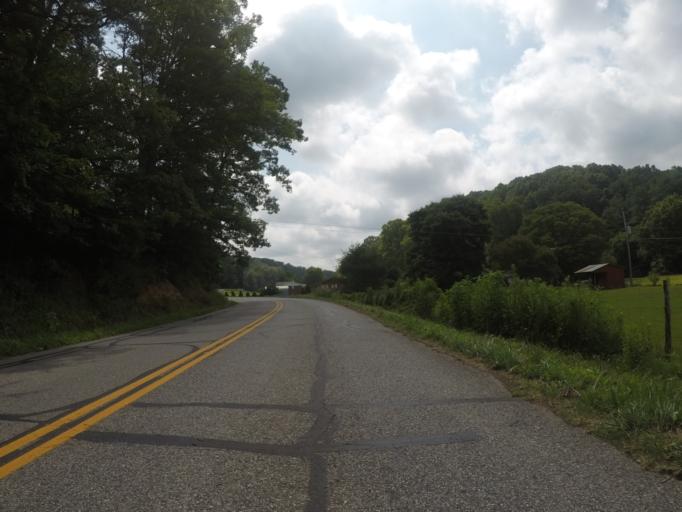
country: US
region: Kentucky
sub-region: Boyd County
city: Meads
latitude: 38.4126
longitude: -82.6773
